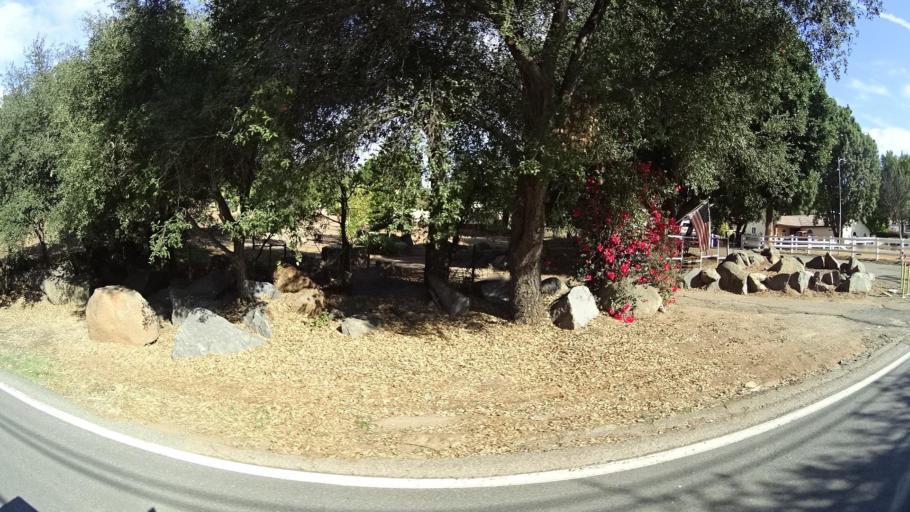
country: US
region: California
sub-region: San Diego County
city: Harbison Canyon
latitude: 32.8190
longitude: -116.8055
